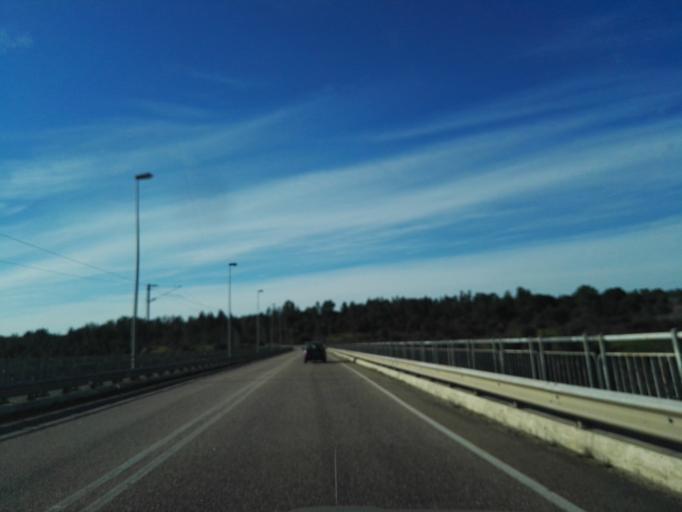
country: PT
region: Santarem
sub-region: Abrantes
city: Alferrarede
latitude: 39.4710
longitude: -8.0654
